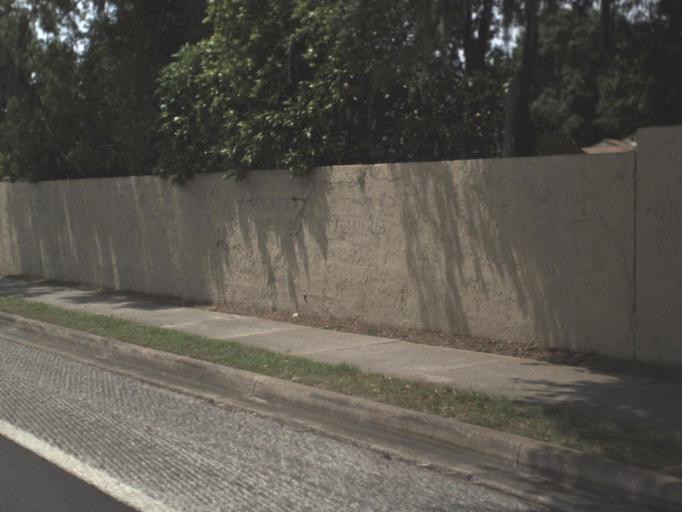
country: US
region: Florida
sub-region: Duval County
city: Jacksonville
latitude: 30.2545
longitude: -81.6413
